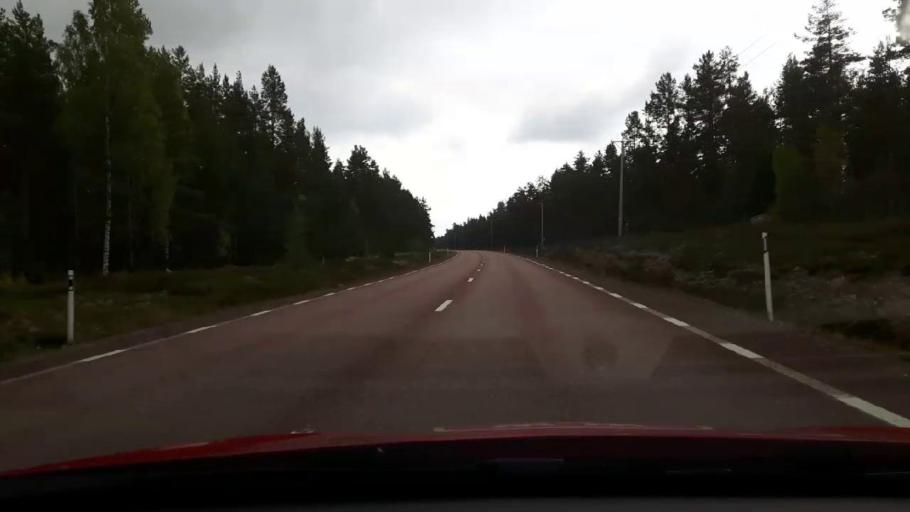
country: SE
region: Gaevleborg
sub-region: Soderhamns Kommun
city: Ljusne
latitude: 61.1097
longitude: 16.9372
